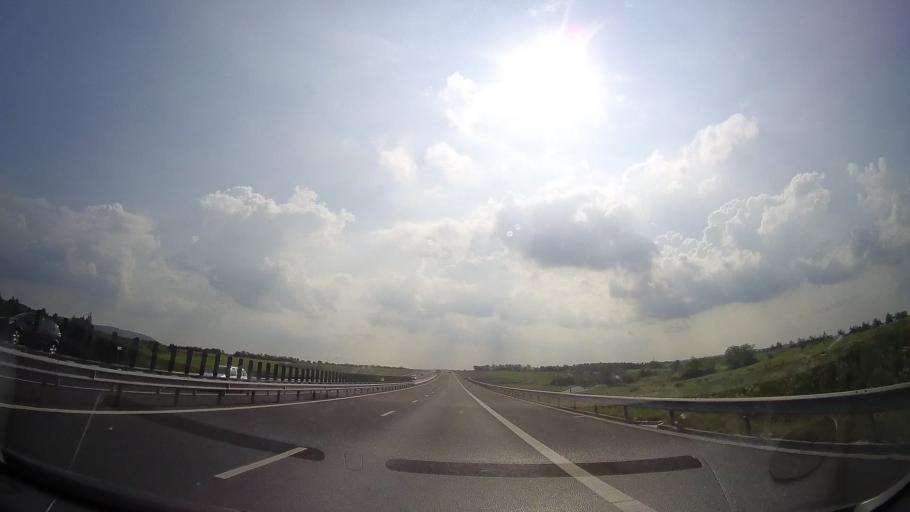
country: RO
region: Timis
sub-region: Comuna Faget
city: Faget
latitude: 45.8192
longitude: 22.1586
